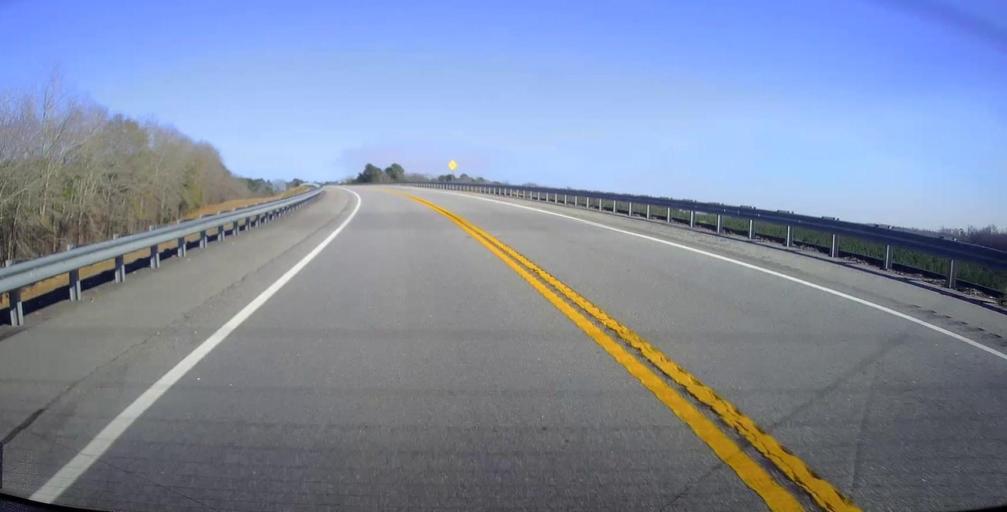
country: US
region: Georgia
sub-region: Macon County
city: Oglethorpe
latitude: 32.3460
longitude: -84.1435
